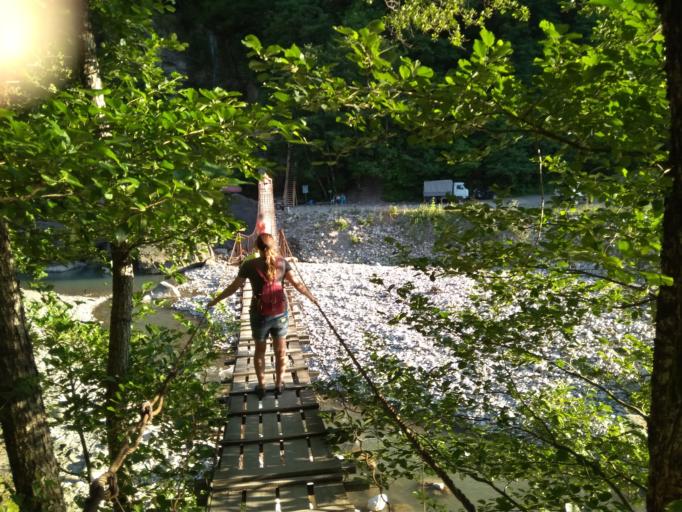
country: RU
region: Krasnodarskiy
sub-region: Sochi City
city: Lazarevskoye
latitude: 43.9995
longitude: 39.3970
